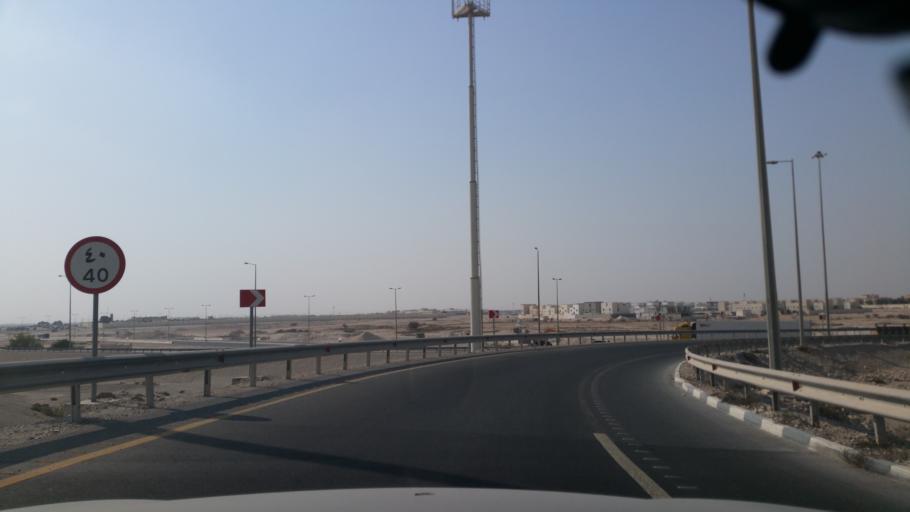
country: QA
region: Baladiyat Umm Salal
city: Umm Salal `Ali
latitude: 25.4483
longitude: 51.4084
